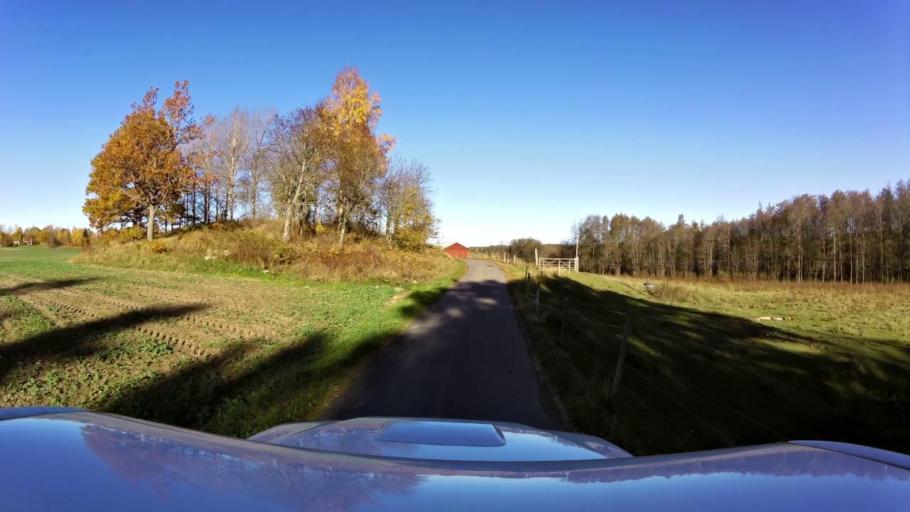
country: SE
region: OEstergoetland
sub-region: Linkopings Kommun
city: Ljungsbro
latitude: 58.5374
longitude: 15.3983
